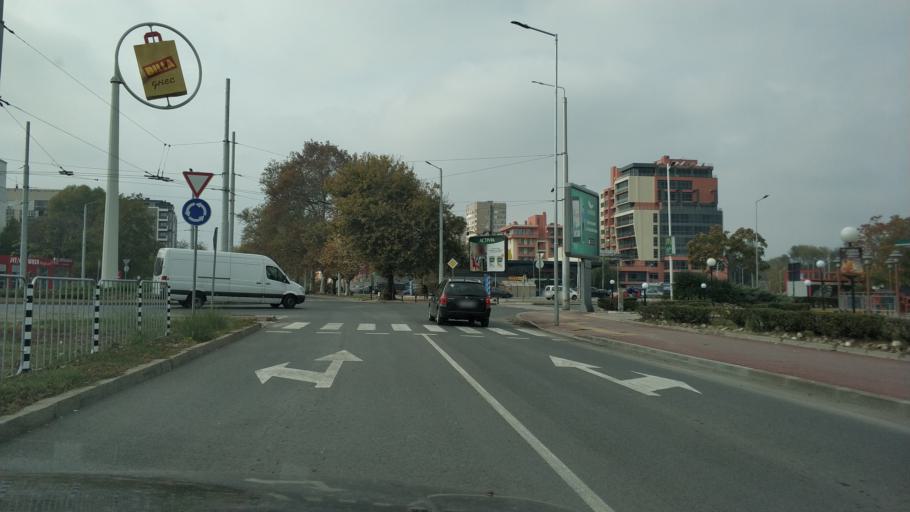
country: BG
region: Plovdiv
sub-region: Obshtina Plovdiv
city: Plovdiv
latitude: 42.1531
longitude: 24.7638
